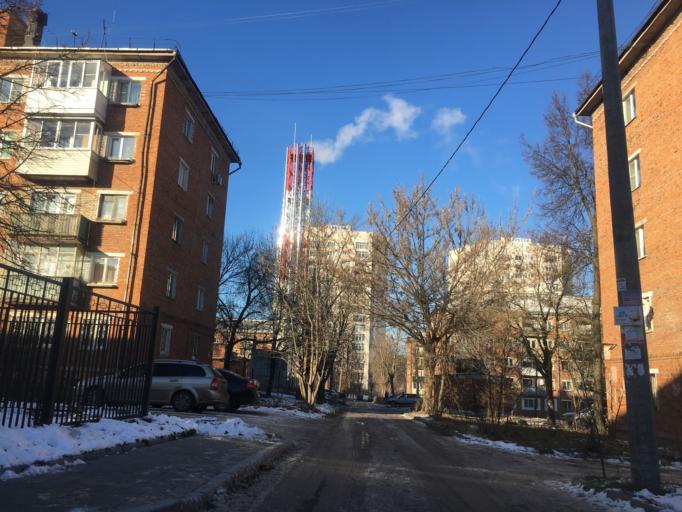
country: RU
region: Tula
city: Mendeleyevskiy
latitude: 54.1741
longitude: 37.5843
